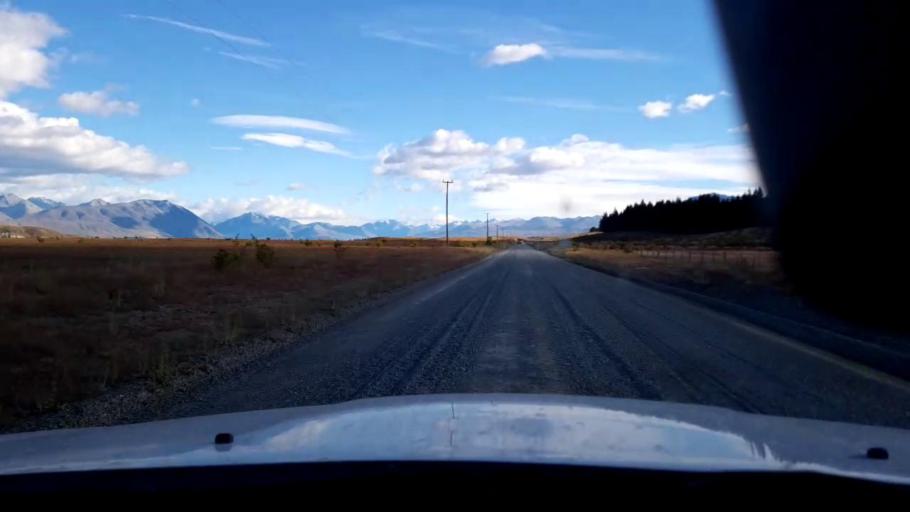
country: NZ
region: Canterbury
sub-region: Timaru District
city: Pleasant Point
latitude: -43.9859
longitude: 170.5057
